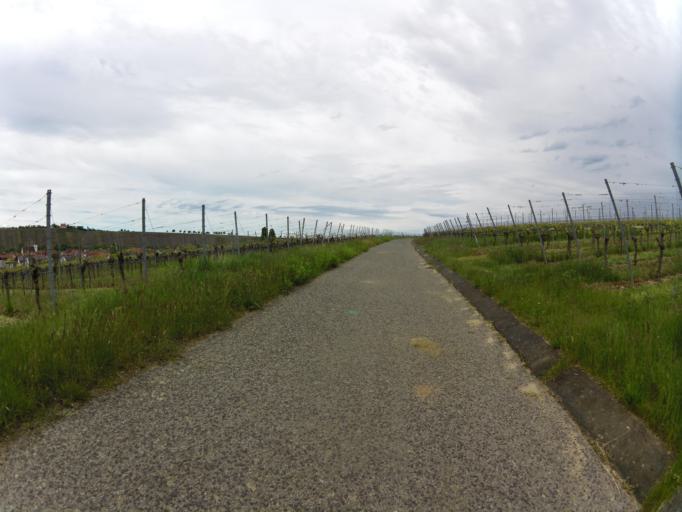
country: DE
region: Bavaria
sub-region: Regierungsbezirk Unterfranken
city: Nordheim
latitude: 49.8544
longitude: 10.1843
